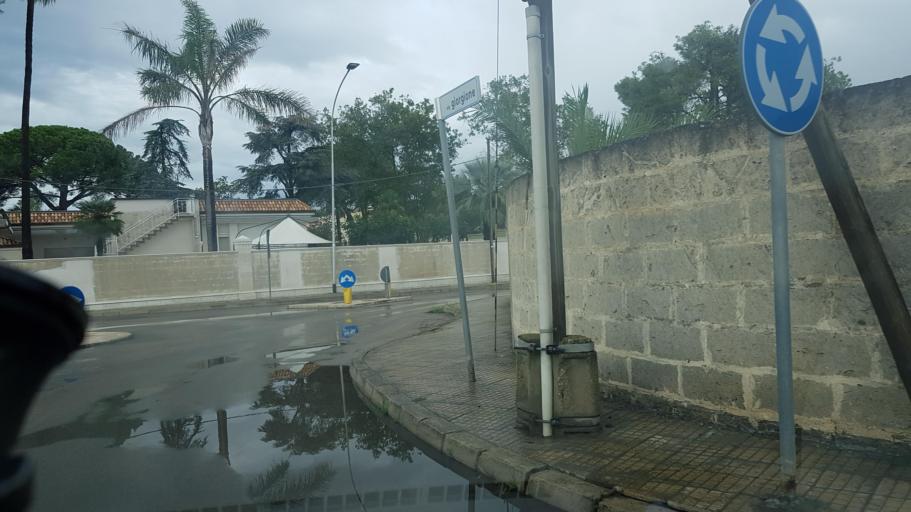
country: IT
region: Apulia
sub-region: Provincia di Lecce
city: Carmiano
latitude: 40.3429
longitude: 18.0493
